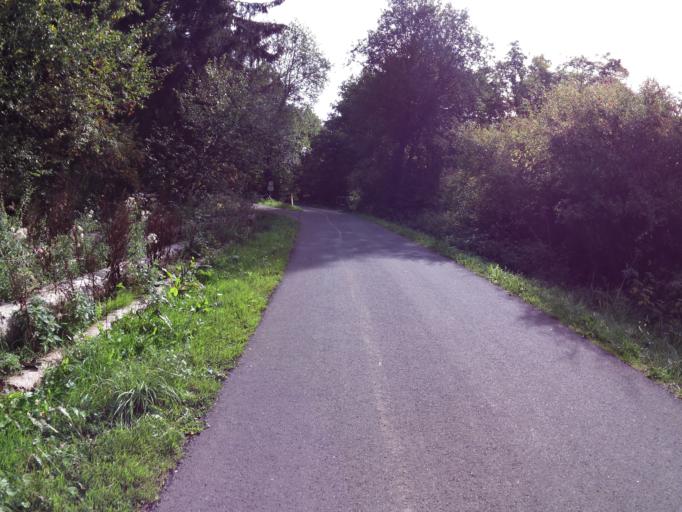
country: DE
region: Rheinland-Pfalz
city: Winterscheid
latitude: 50.2334
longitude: 6.2609
